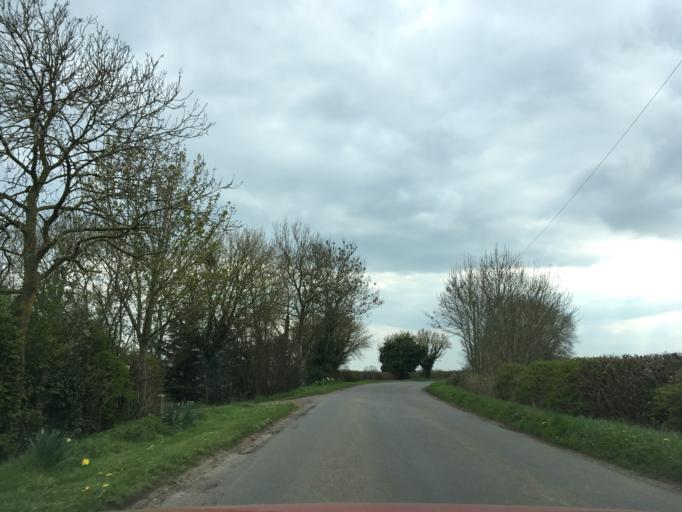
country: GB
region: England
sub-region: Oxfordshire
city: Bicester
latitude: 51.9372
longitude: -1.1375
